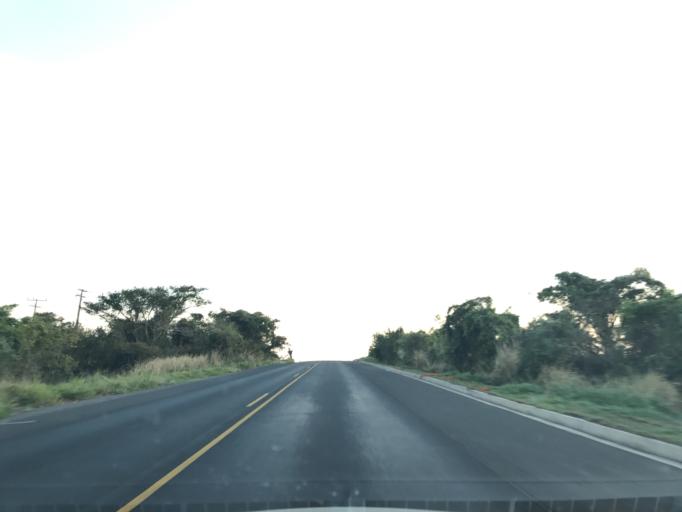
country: BR
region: Sao Paulo
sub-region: Pirapozinho
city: Pirapozinho
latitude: -22.4098
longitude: -51.6291
